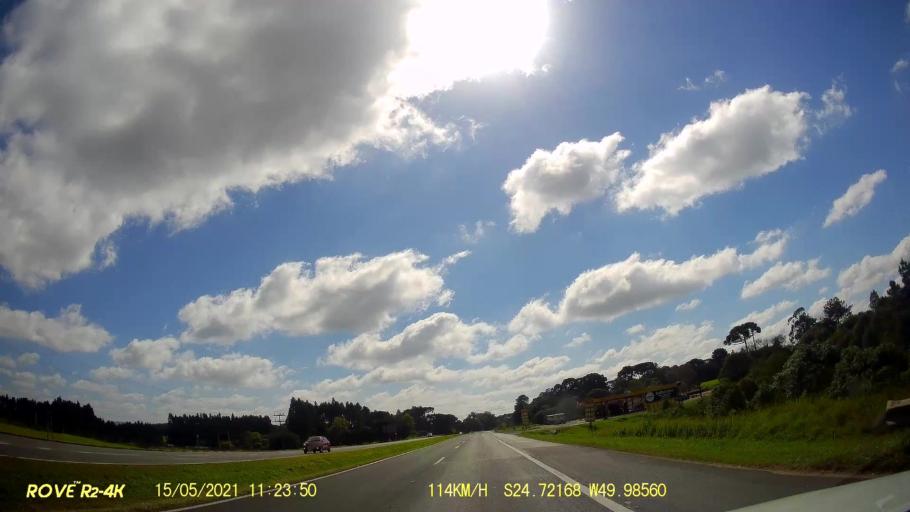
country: BR
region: Parana
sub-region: Castro
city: Castro
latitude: -24.7218
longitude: -49.9857
